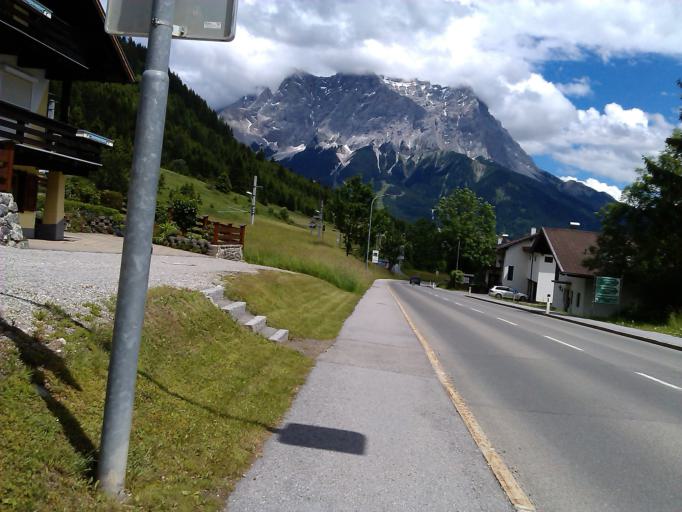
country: AT
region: Tyrol
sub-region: Politischer Bezirk Reutte
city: Lermoos
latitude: 47.4054
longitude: 10.8737
